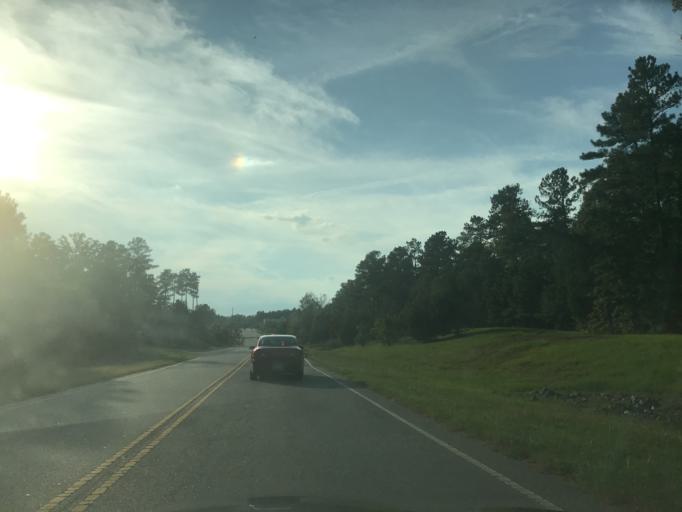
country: US
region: North Carolina
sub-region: Wake County
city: Morrisville
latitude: 35.8605
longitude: -78.8904
